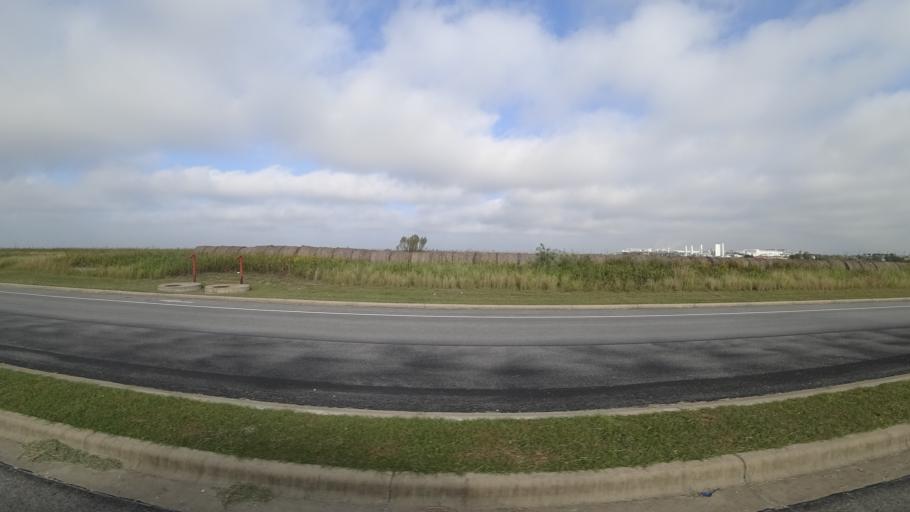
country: US
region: Texas
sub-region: Travis County
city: Pflugerville
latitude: 30.3639
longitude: -97.6366
